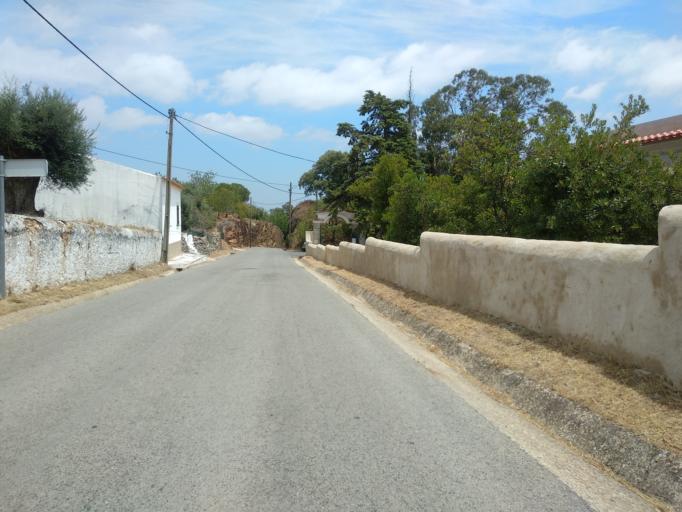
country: PT
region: Faro
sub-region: Sao Bras de Alportel
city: Sao Bras de Alportel
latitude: 37.1635
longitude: -7.8917
